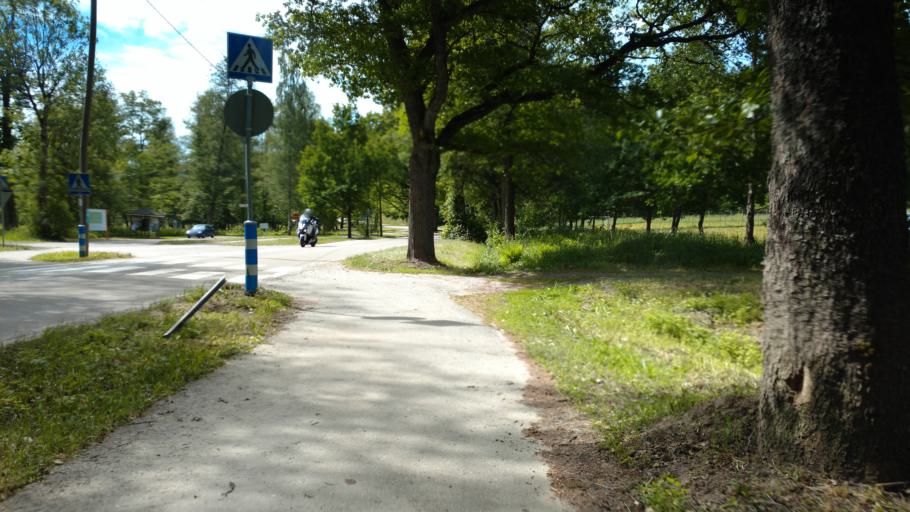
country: FI
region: Uusimaa
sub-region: Raaseporin
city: Pohja
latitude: 60.1256
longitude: 23.5367
